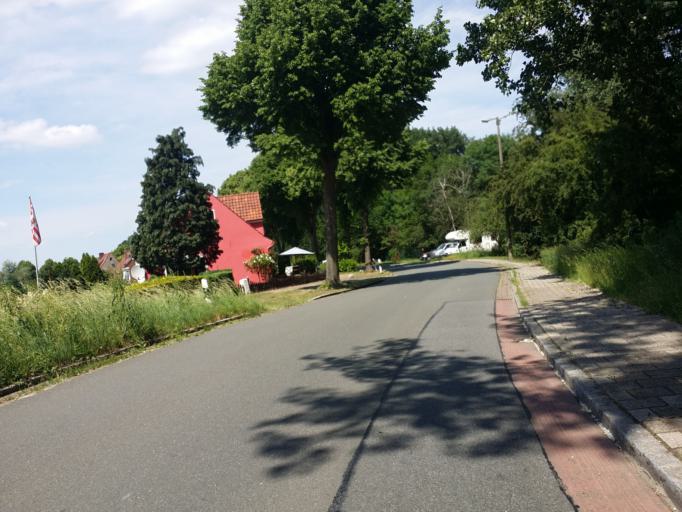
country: DE
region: Lower Saxony
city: Ritterhude
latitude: 53.1136
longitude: 8.7057
